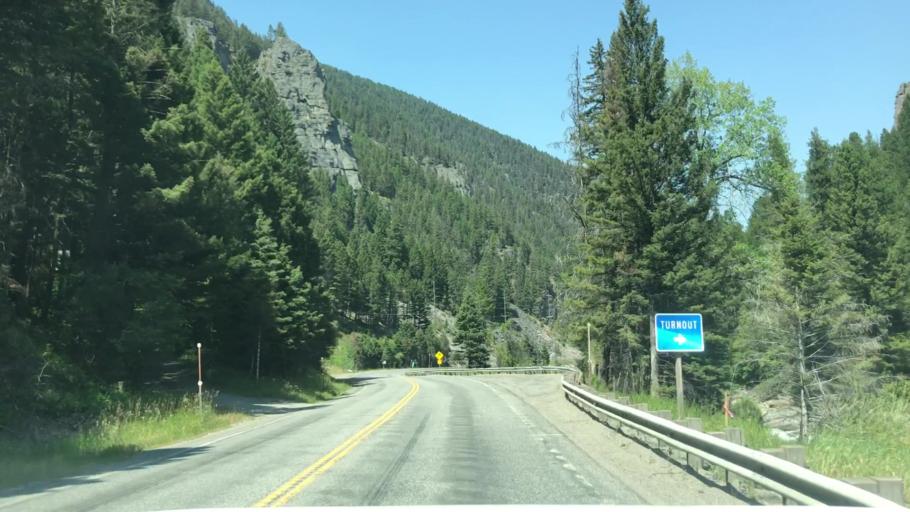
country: US
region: Montana
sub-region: Gallatin County
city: Big Sky
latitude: 45.4144
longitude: -111.2311
